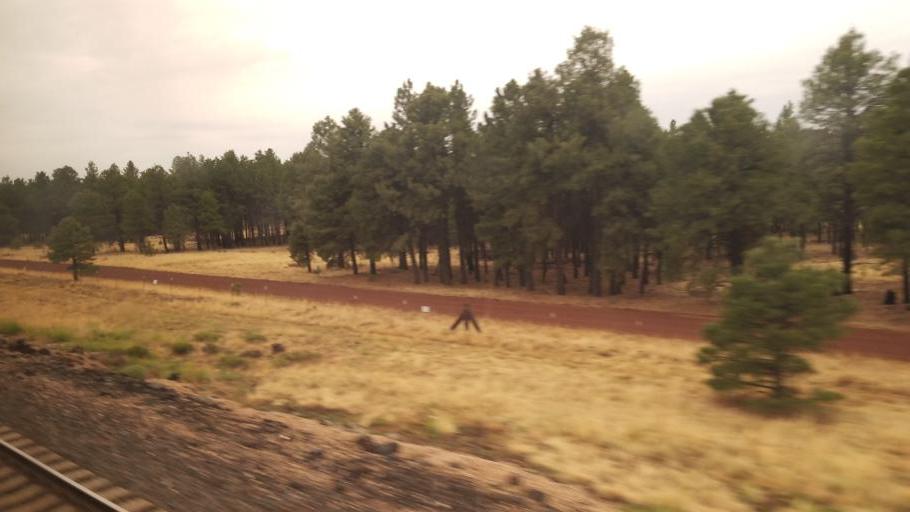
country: US
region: Arizona
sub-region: Coconino County
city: Flagstaff
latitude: 35.2194
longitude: -111.7932
